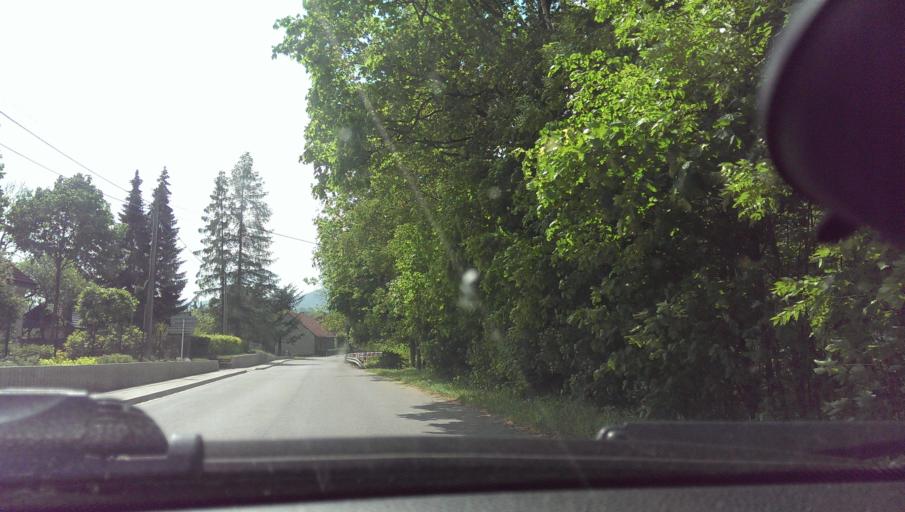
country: CZ
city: Lichnov (o. Novy Jicin)
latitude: 49.5738
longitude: 18.1813
